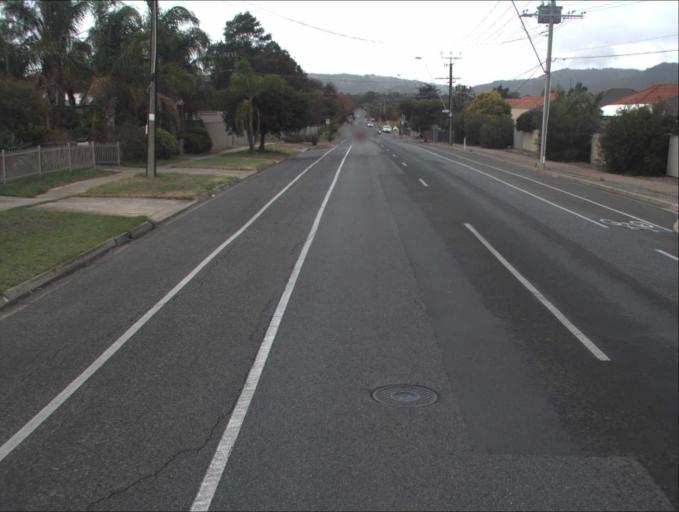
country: AU
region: South Australia
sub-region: Campbelltown
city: Paradise
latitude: -34.8573
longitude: 138.6680
